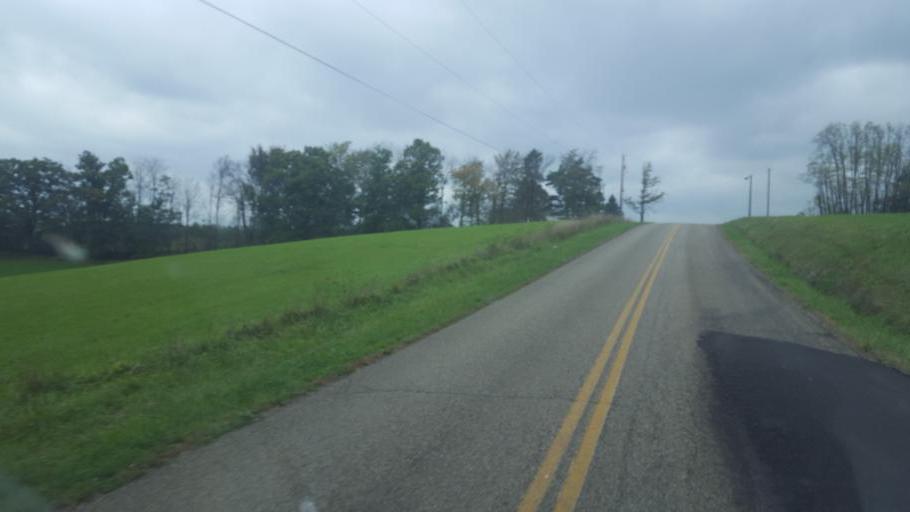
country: US
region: Ohio
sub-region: Carroll County
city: Carrollton
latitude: 40.5343
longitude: -81.1608
